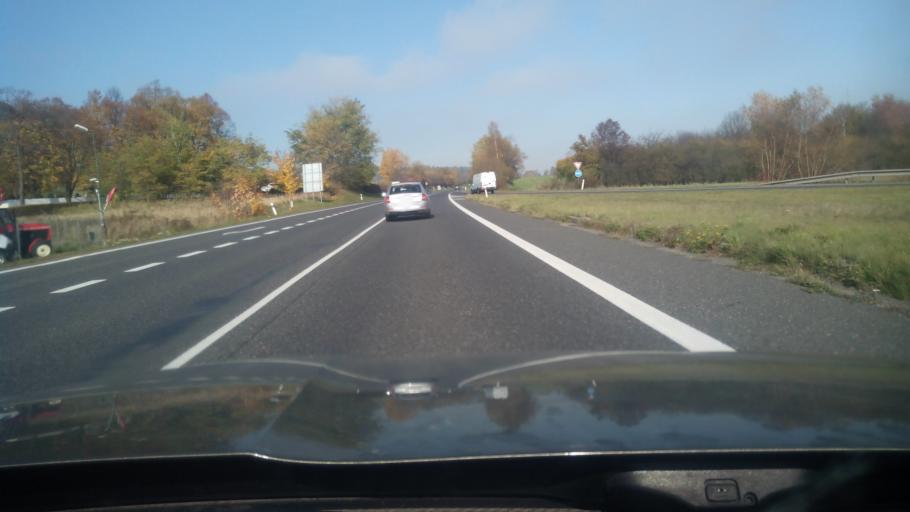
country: CZ
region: Central Bohemia
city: Milin
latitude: 49.6399
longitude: 14.0505
